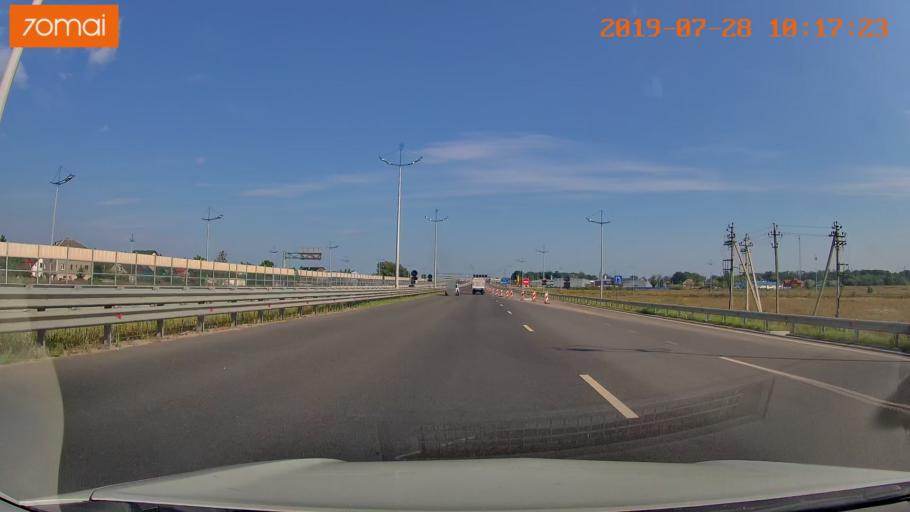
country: RU
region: Kaliningrad
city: Maloye Isakovo
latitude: 54.7393
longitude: 20.5946
